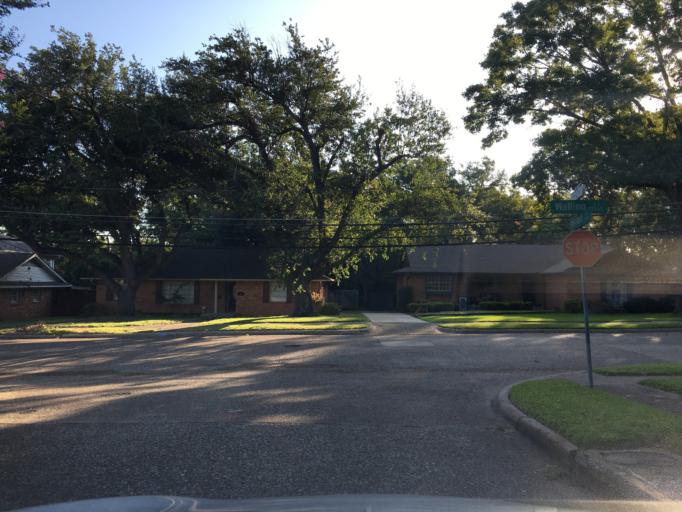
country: US
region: Texas
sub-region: Dallas County
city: Highland Park
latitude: 32.8620
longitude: -96.7380
